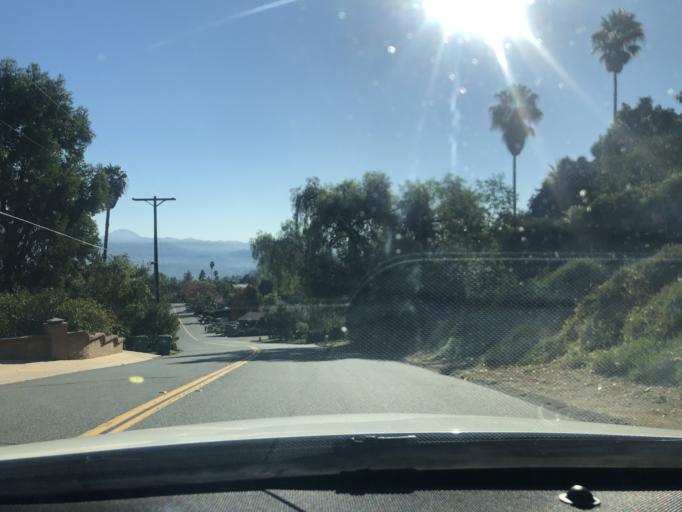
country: US
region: California
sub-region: San Diego County
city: Casa de Oro-Mount Helix
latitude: 32.7712
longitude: -116.9498
